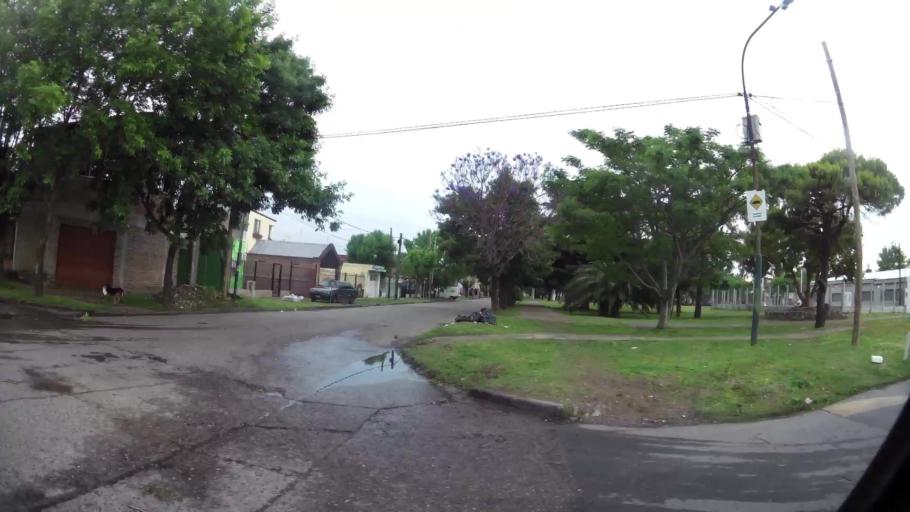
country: AR
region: Buenos Aires
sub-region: Partido de Lomas de Zamora
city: Lomas de Zamora
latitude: -34.7438
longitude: -58.3455
